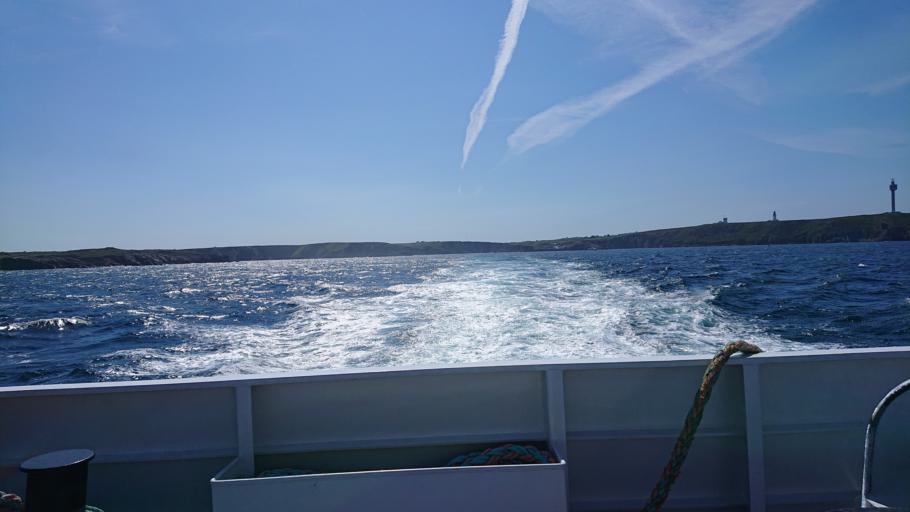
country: FR
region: Brittany
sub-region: Departement du Finistere
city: Porspoder
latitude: 48.4702
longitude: -5.0323
